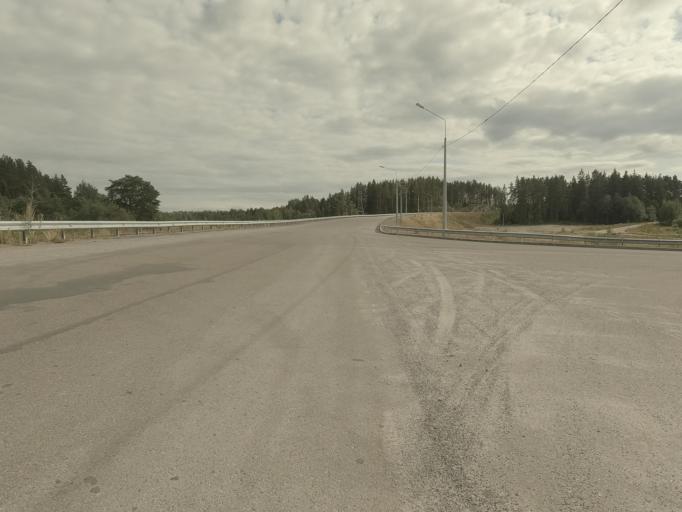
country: RU
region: Leningrad
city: Kamennogorsk
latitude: 60.9646
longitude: 29.1411
